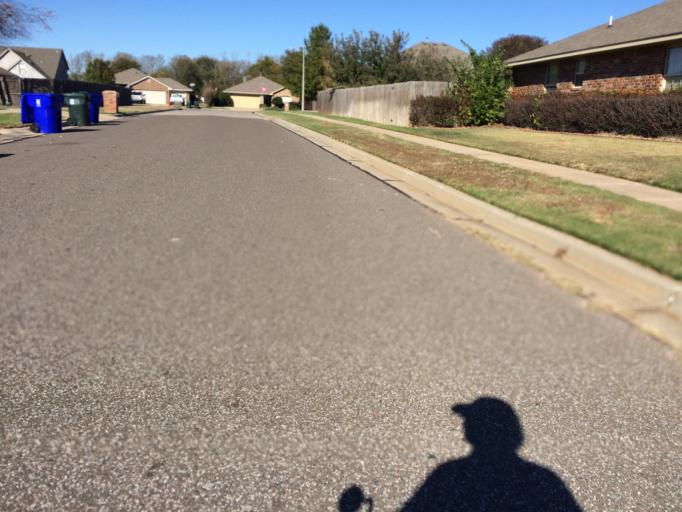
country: US
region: Oklahoma
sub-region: Cleveland County
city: Noble
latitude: 35.1684
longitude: -97.4260
